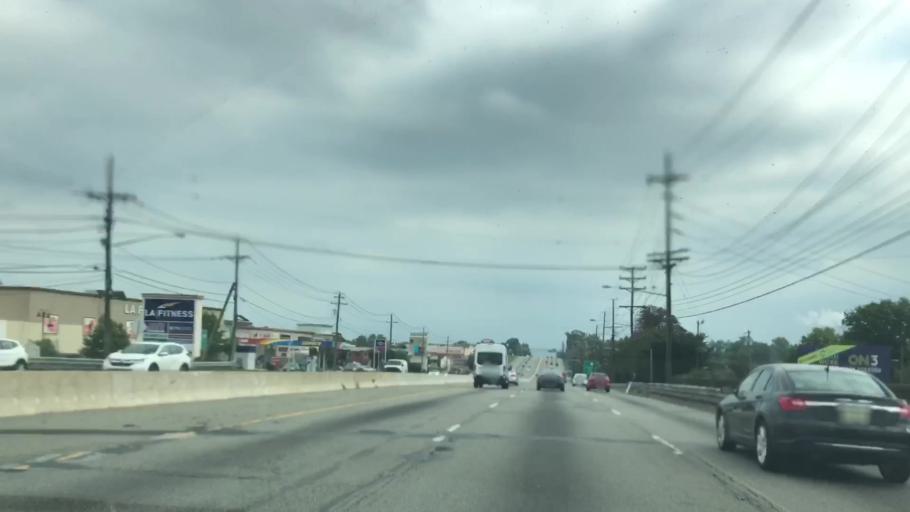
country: US
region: New Jersey
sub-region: Essex County
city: Nutley
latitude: 40.8390
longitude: -74.1582
